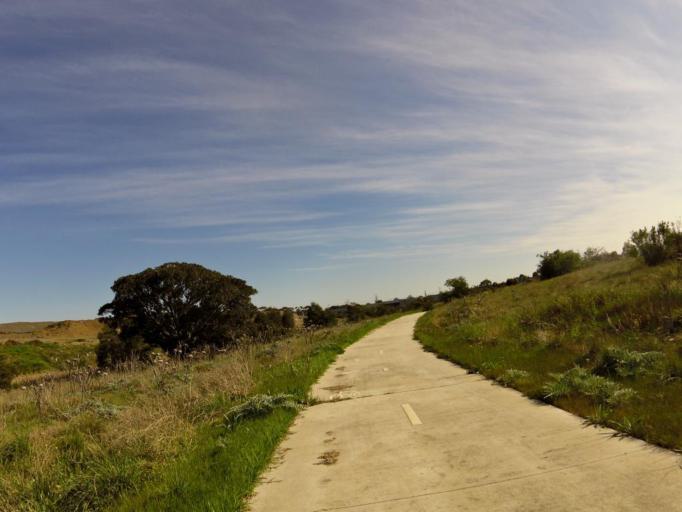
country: AU
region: Victoria
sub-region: Brimbank
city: Brooklyn
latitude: -37.8154
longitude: 144.8283
